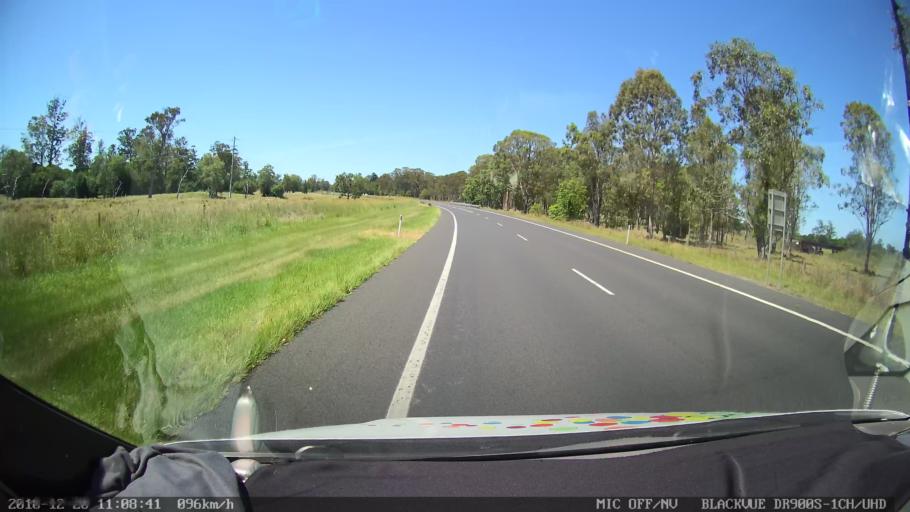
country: AU
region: New South Wales
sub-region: Richmond Valley
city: Casino
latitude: -28.9256
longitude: 153.0049
